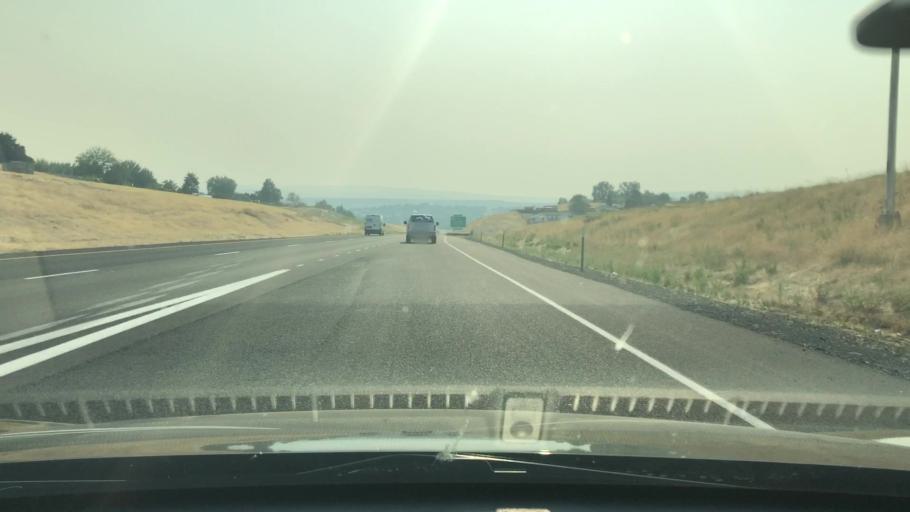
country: US
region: Oregon
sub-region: Umatilla County
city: Pendleton
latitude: 45.6628
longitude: -118.7834
